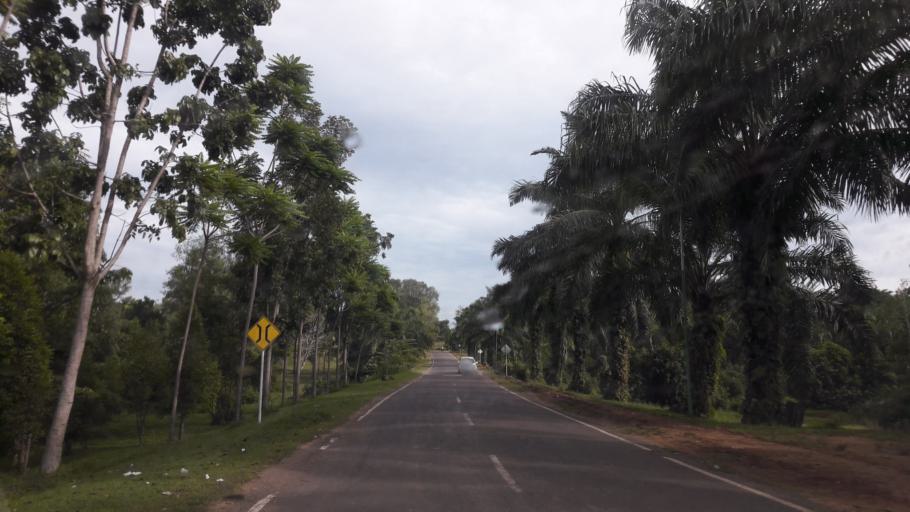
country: ID
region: South Sumatra
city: Gunungmegang Dalam
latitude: -3.2657
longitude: 103.8274
